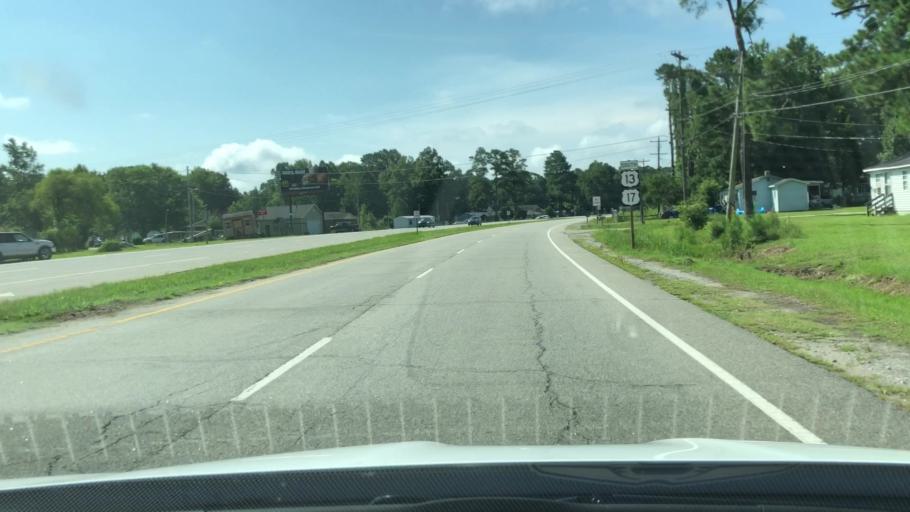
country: US
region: North Carolina
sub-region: Bertie County
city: Windsor
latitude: 35.9649
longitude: -76.9521
